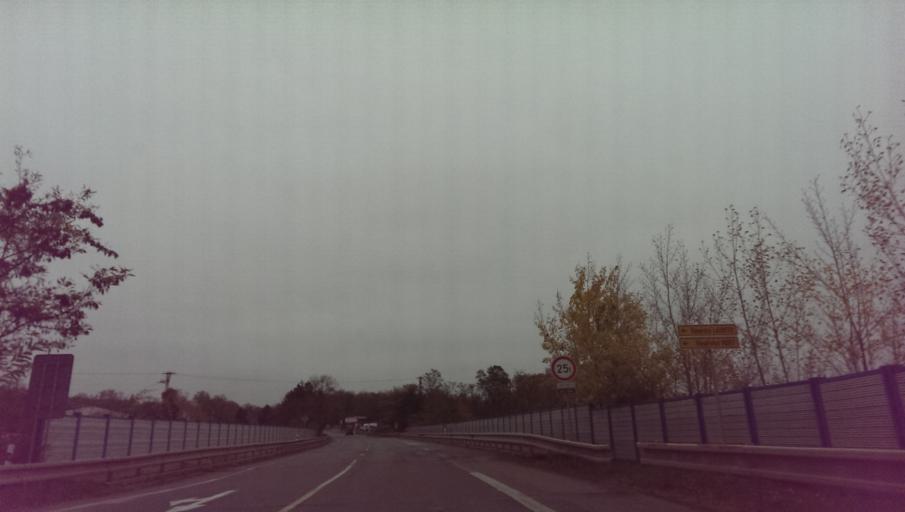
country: CZ
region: South Moravian
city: Dobsice
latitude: 48.8516
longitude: 16.0888
